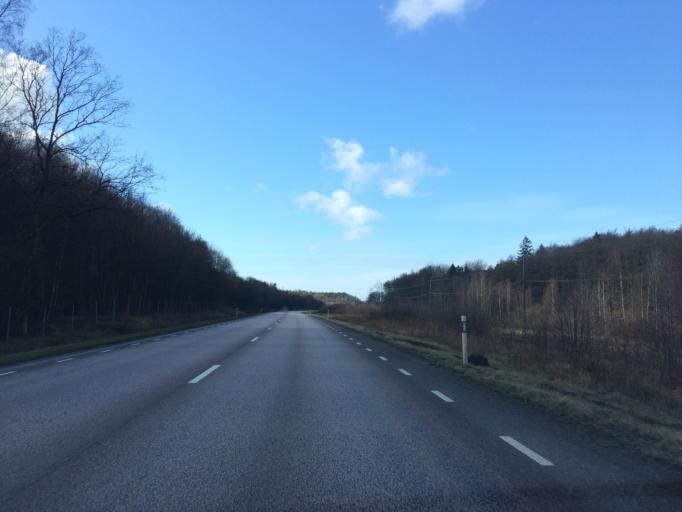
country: SE
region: Halland
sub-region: Laholms Kommun
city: Knared
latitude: 56.5174
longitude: 13.3004
